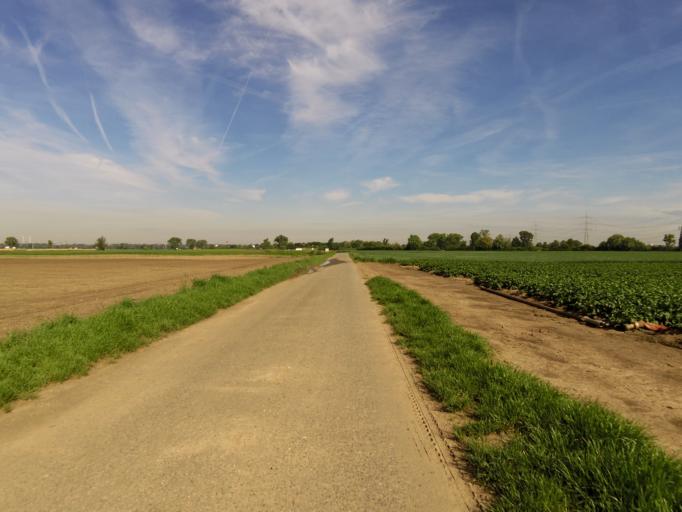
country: DE
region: Hesse
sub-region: Regierungsbezirk Darmstadt
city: Burstadt
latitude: 49.6482
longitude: 8.4374
